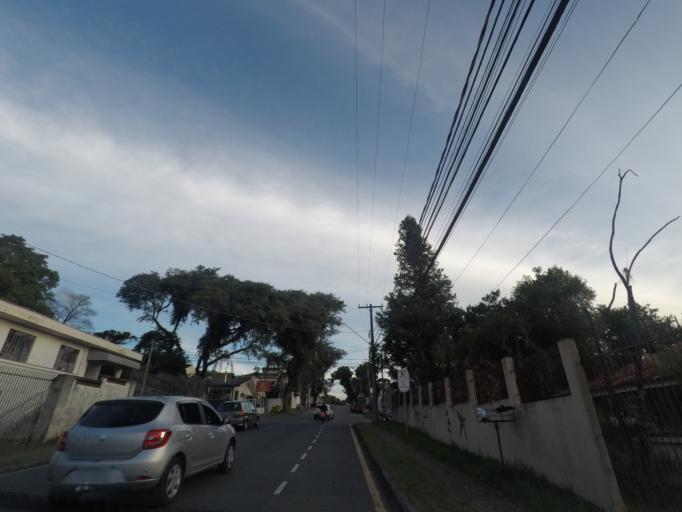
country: BR
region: Parana
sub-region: Curitiba
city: Curitiba
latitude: -25.4178
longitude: -49.2822
